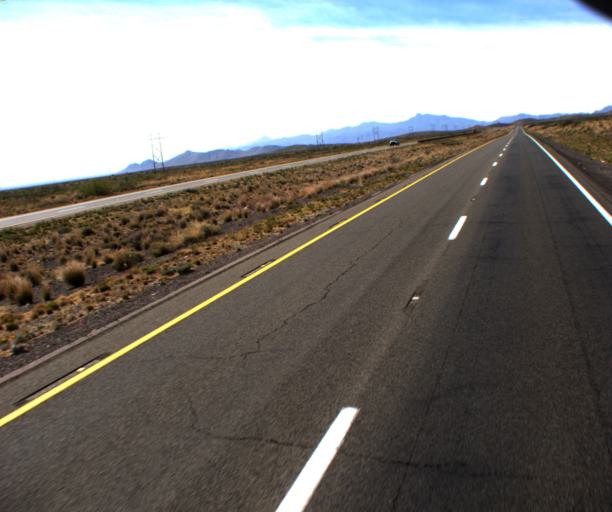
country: US
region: Arizona
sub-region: Graham County
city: Swift Trail Junction
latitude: 32.5008
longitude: -109.6741
